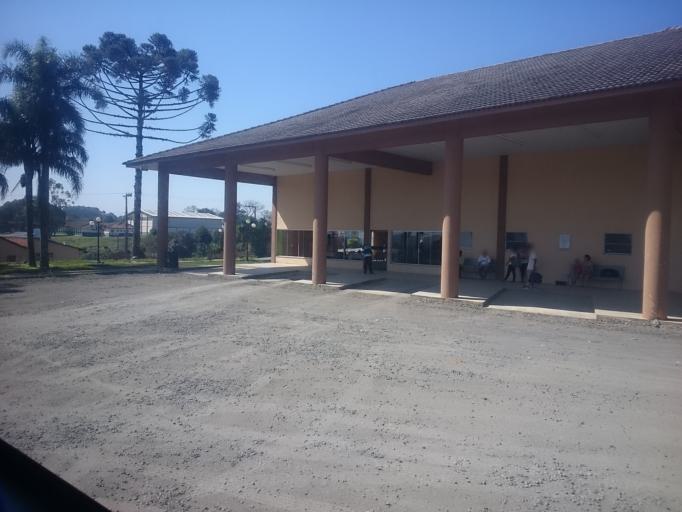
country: BR
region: Santa Catarina
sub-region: Canoinhas
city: Canoinhas
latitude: -26.4620
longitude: -50.2266
